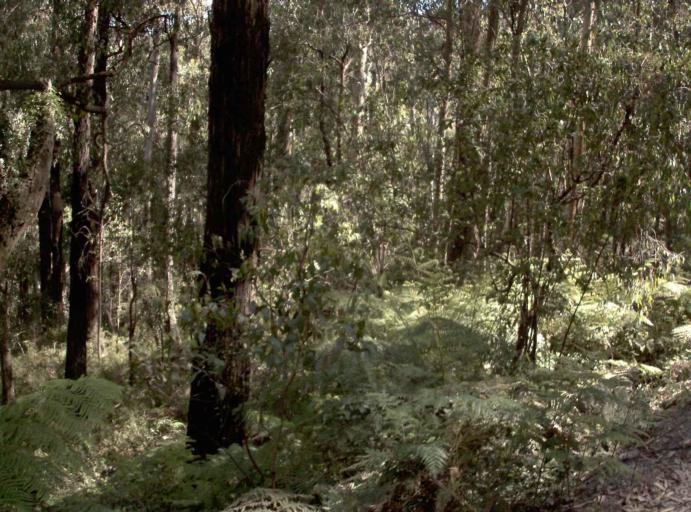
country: AU
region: New South Wales
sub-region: Bombala
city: Bombala
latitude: -37.2504
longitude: 148.7424
